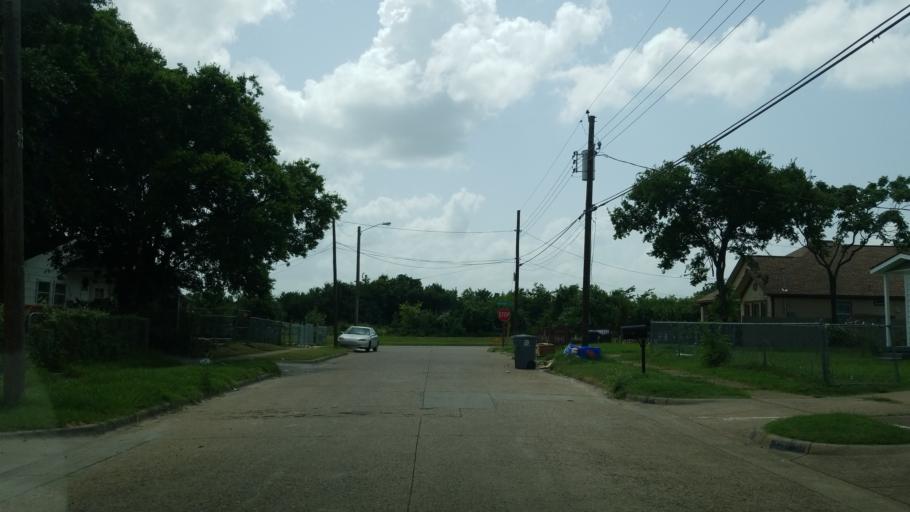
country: US
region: Texas
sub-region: Dallas County
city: Cockrell Hill
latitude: 32.7847
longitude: -96.8819
